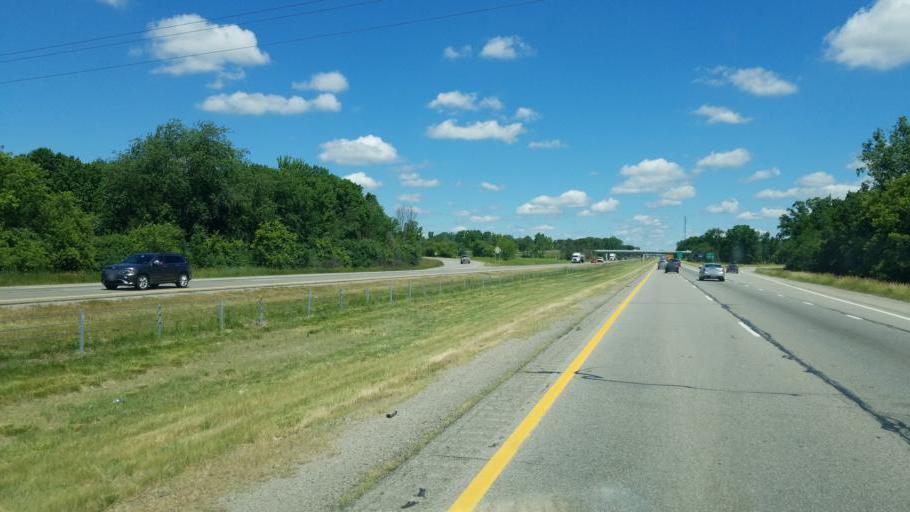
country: US
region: Michigan
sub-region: Washtenaw County
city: Ypsilanti
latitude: 42.2010
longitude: -83.6848
